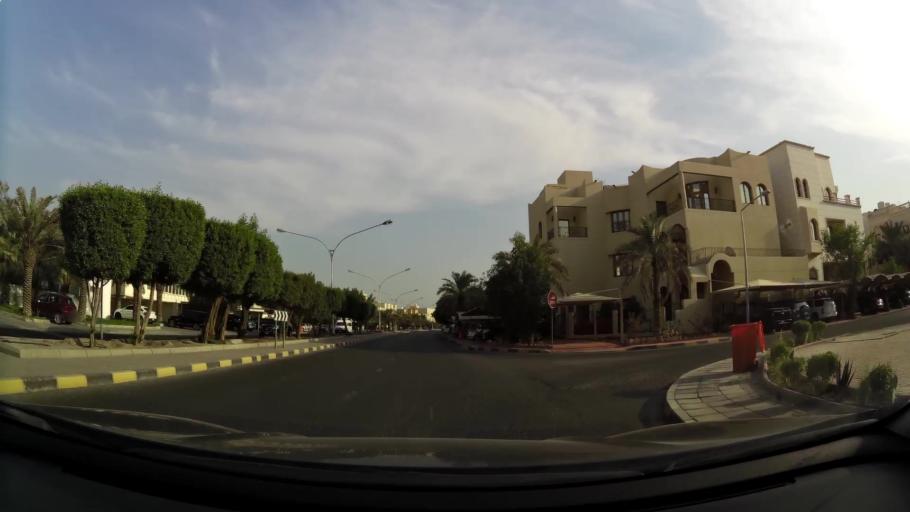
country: KW
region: Muhafazat Hawalli
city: Hawalli
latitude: 29.3122
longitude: 48.0127
